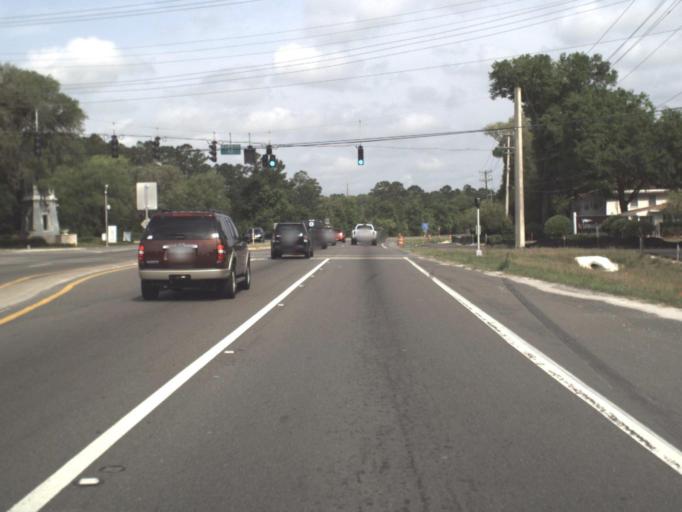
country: US
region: Florida
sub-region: Clay County
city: Green Cove Springs
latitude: 30.0086
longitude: -81.6952
